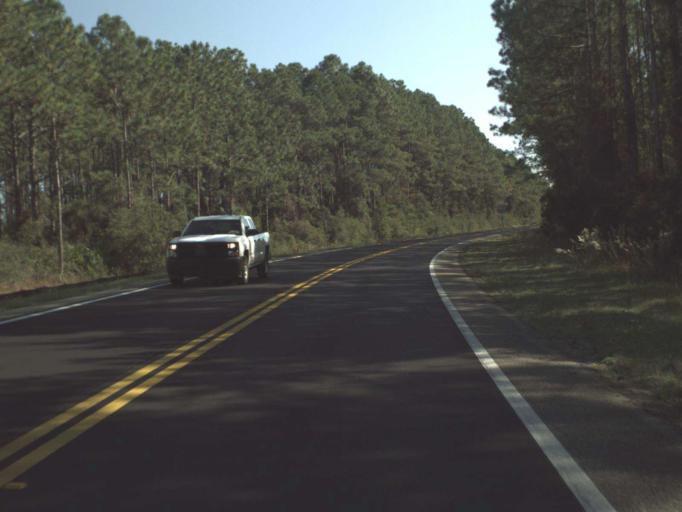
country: US
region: Florida
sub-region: Gulf County
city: Port Saint Joe
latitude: 29.7746
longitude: -85.2672
